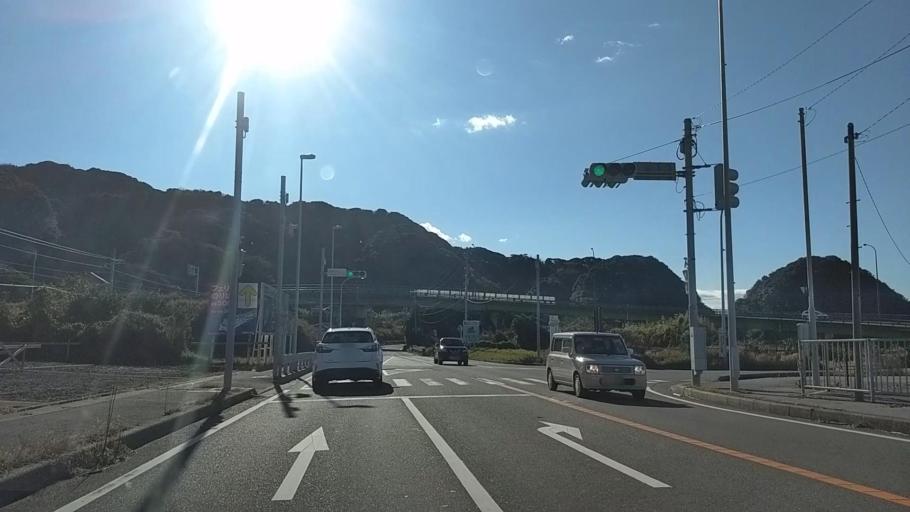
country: JP
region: Chiba
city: Futtsu
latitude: 35.1751
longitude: 139.8188
